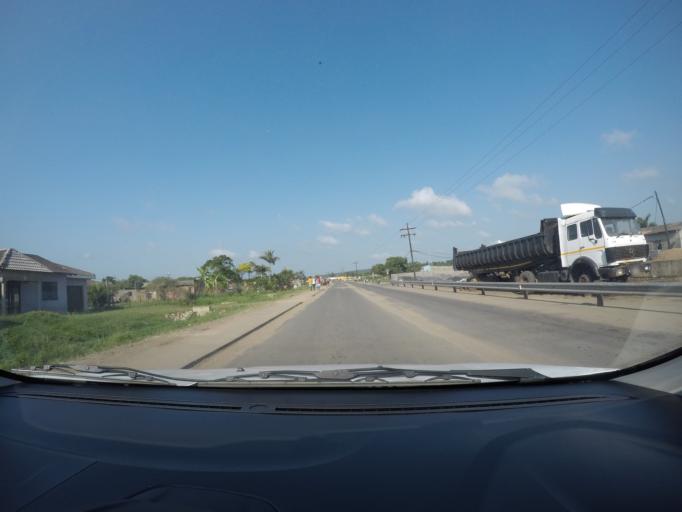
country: ZA
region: KwaZulu-Natal
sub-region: uThungulu District Municipality
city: eSikhawini
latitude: -28.8570
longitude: 31.9269
